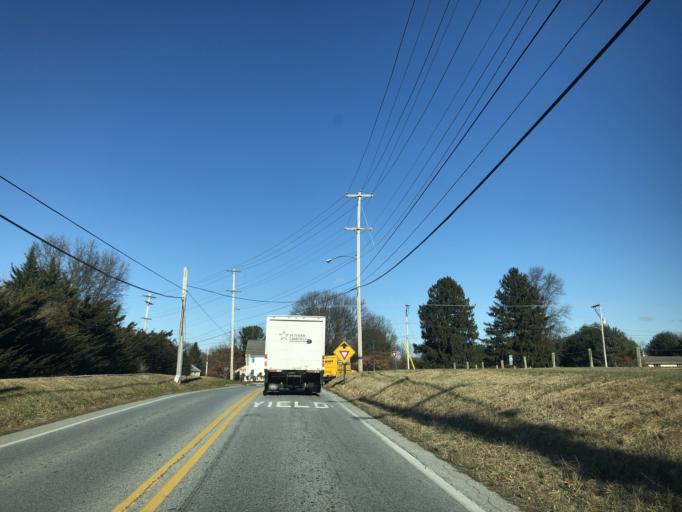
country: US
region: Pennsylvania
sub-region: Chester County
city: Kennett Square
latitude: 39.8906
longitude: -75.7222
